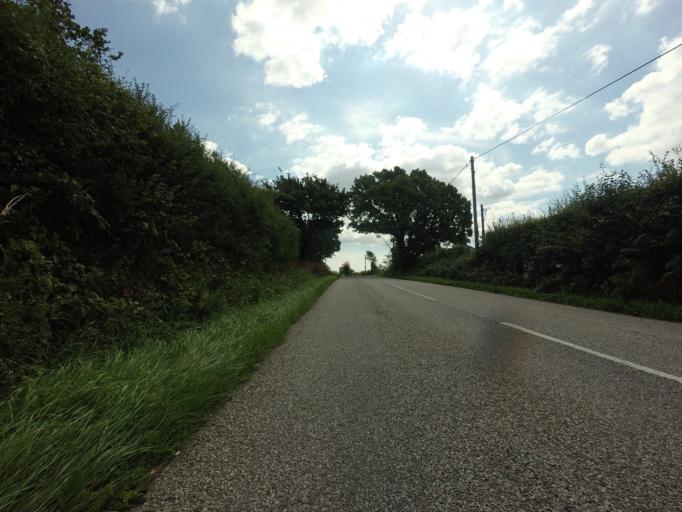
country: GB
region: England
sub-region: Kent
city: Tenterden
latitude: 51.0714
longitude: 0.7474
